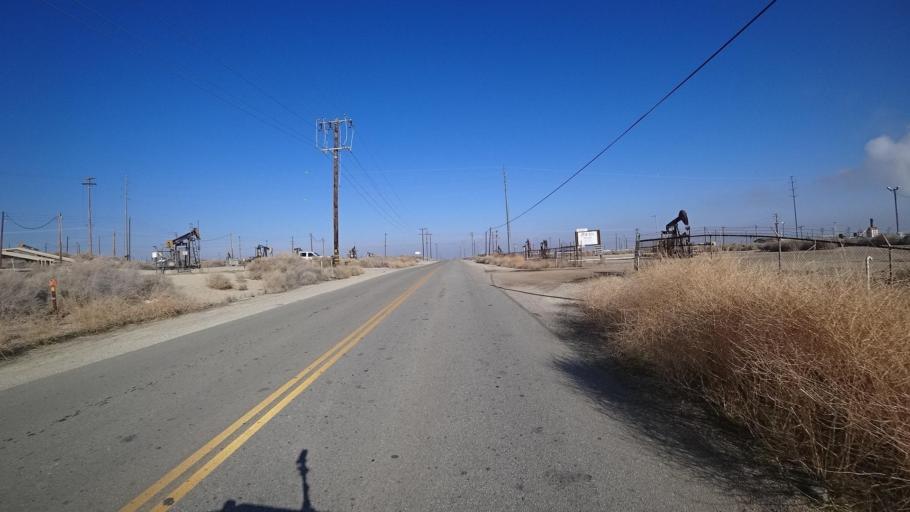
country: US
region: California
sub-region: Kern County
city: Taft Heights
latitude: 35.2079
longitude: -119.5982
